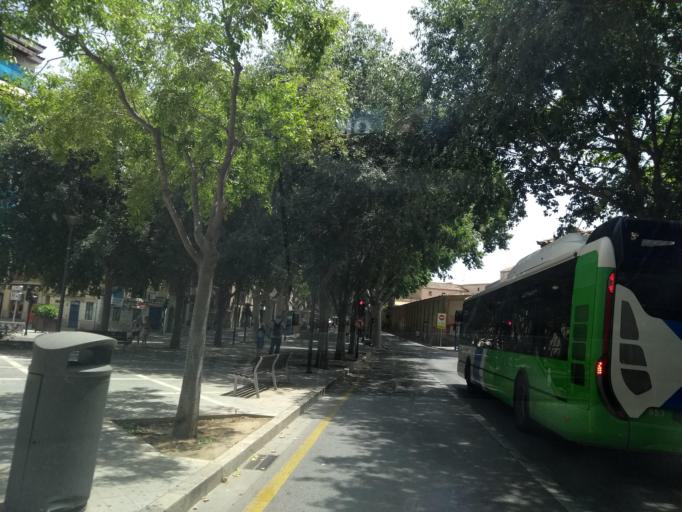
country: ES
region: Balearic Islands
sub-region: Illes Balears
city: Palma
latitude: 39.5752
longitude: 2.6478
